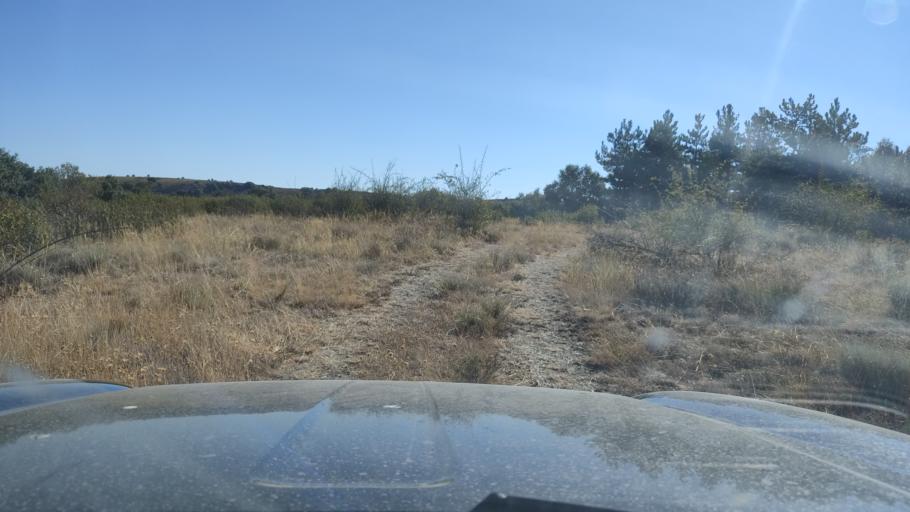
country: ES
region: Aragon
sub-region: Provincia de Teruel
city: Monforte de Moyuela
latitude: 41.0215
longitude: -1.0073
